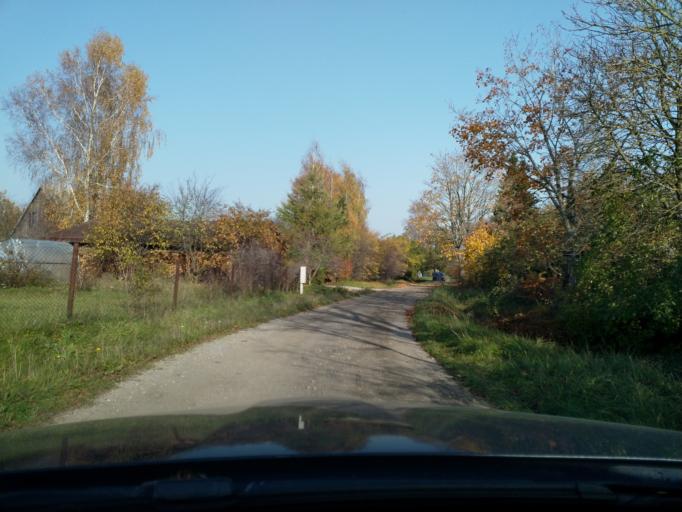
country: LV
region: Kuldigas Rajons
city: Kuldiga
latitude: 56.9606
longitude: 21.9874
